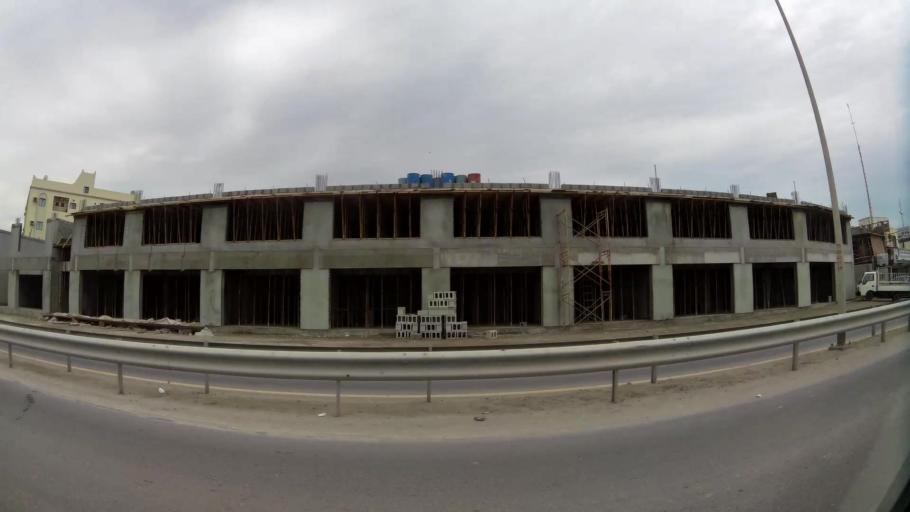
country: BH
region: Northern
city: Sitrah
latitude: 26.1530
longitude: 50.6207
